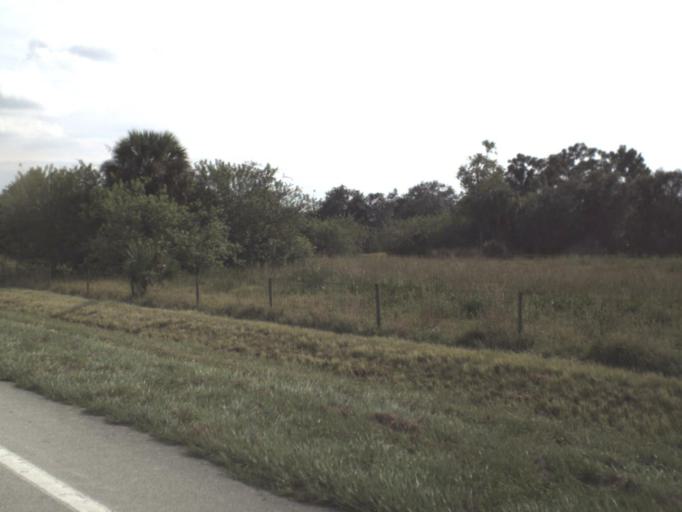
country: US
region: Florida
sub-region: Okeechobee County
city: Taylor Creek
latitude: 27.2264
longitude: -80.7699
